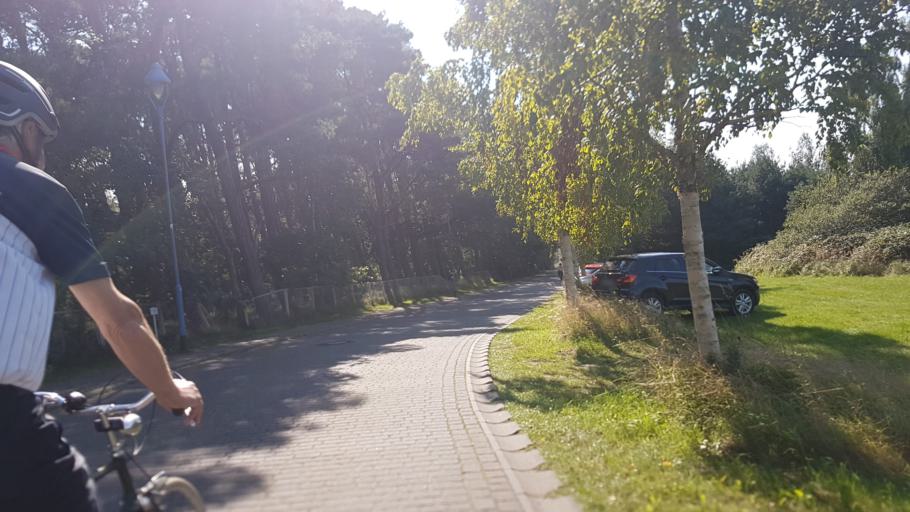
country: DE
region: Mecklenburg-Vorpommern
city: Ostseebad Gohren
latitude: 54.3289
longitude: 13.7290
